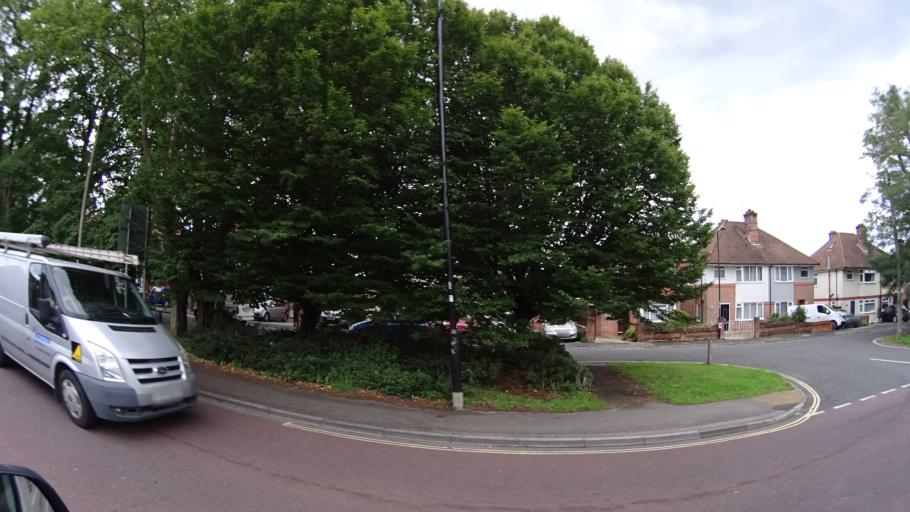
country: GB
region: England
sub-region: Hampshire
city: West End
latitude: 50.9146
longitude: -1.3543
